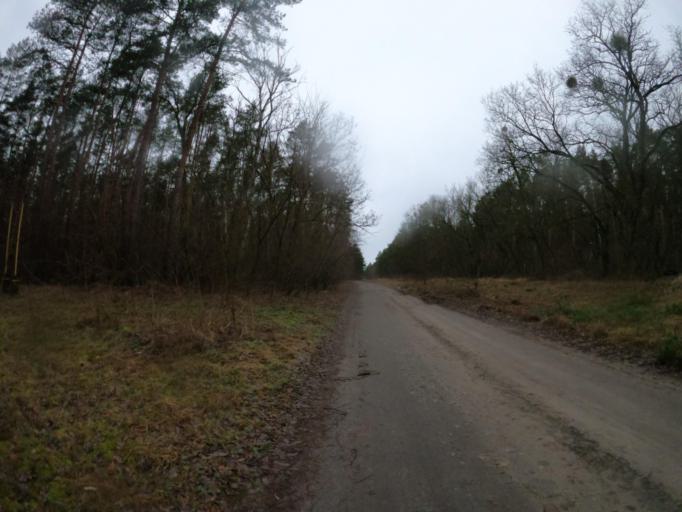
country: PL
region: West Pomeranian Voivodeship
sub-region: Powiat mysliborski
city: Debno
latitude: 52.7978
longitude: 14.7549
